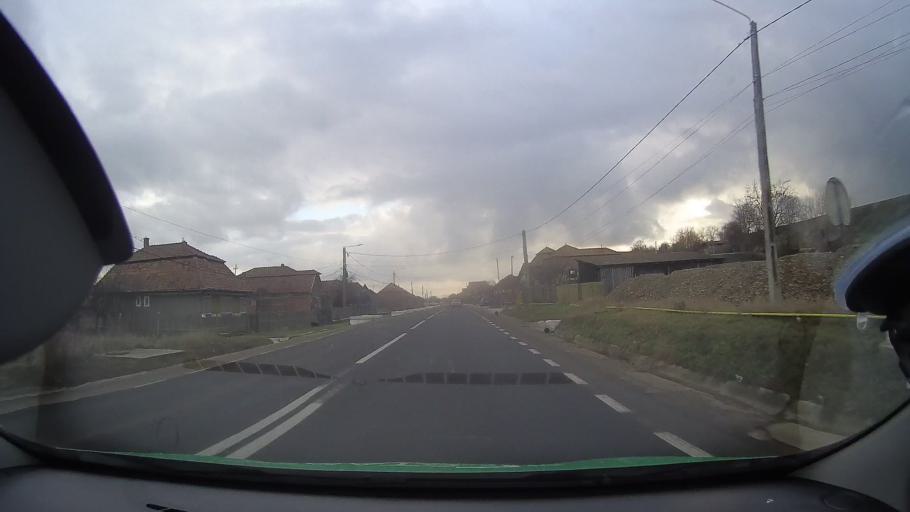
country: RO
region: Cluj
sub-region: Comuna Viisoara
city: Viisoara
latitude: 46.5151
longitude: 23.9164
